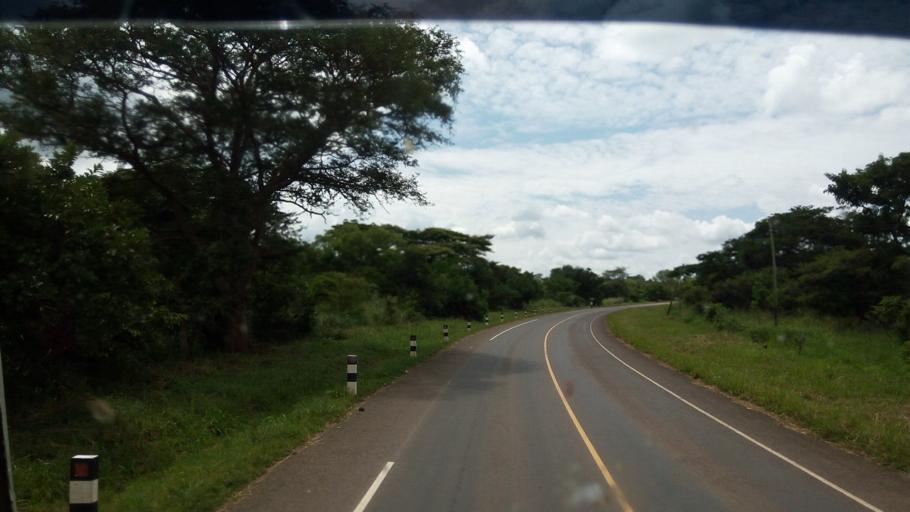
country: UG
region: Northern Region
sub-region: Oyam District
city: Oyam
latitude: 2.2501
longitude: 32.2353
